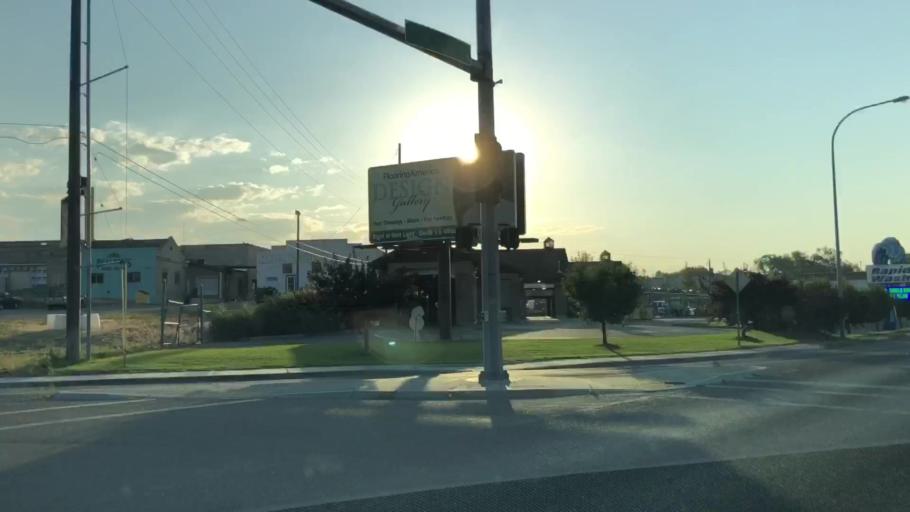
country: US
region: Idaho
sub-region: Bonneville County
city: Idaho Falls
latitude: 43.4844
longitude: -112.0472
